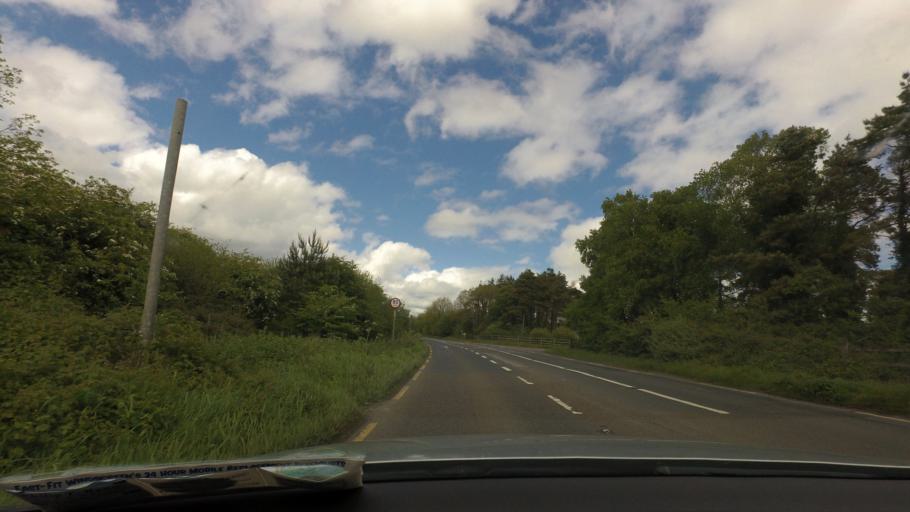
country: IE
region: Munster
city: Cashel
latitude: 52.5815
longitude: -7.8238
